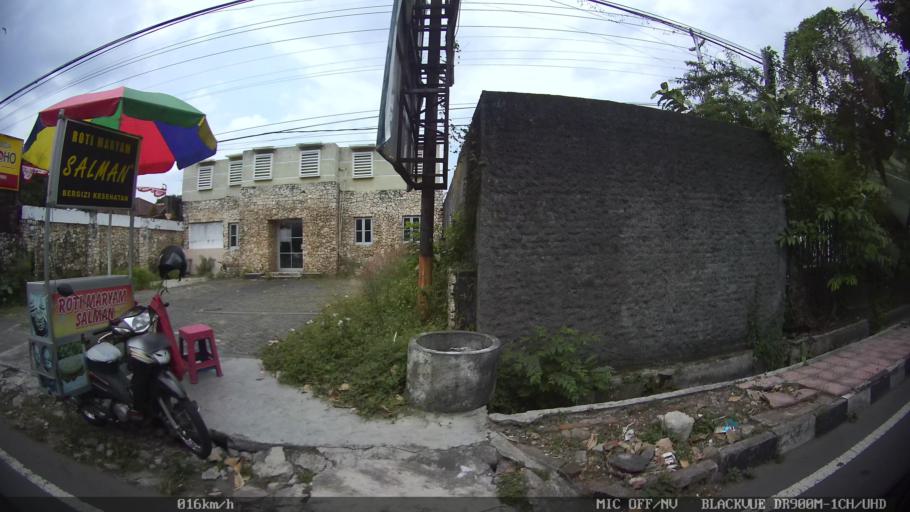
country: ID
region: Daerah Istimewa Yogyakarta
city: Yogyakarta
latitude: -7.7956
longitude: 110.3929
